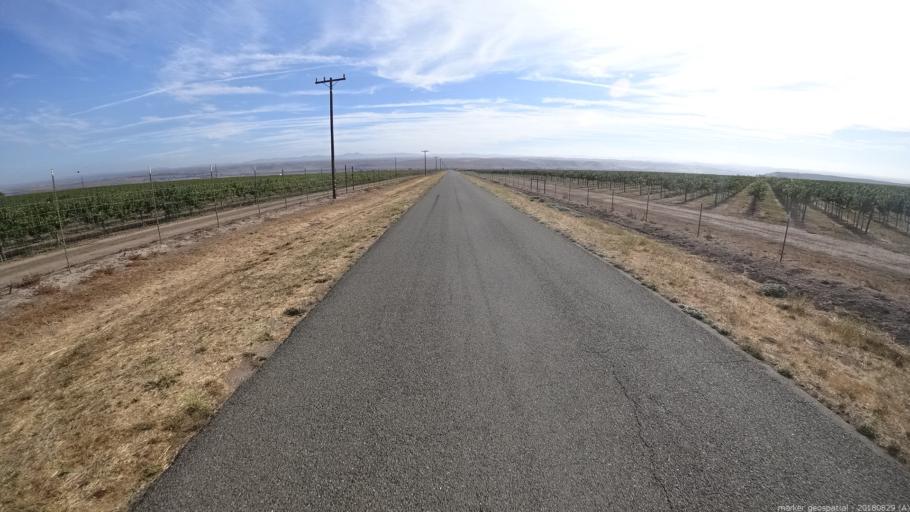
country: US
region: California
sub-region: Monterey County
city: King City
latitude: 36.0874
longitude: -121.0311
